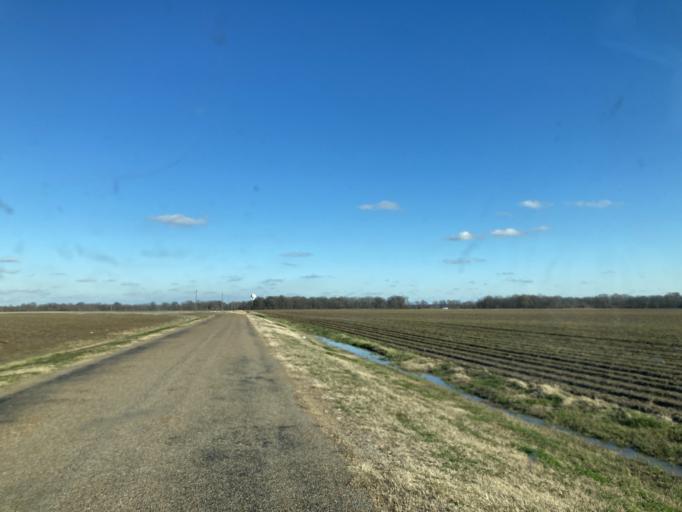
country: US
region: Mississippi
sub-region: Yazoo County
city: Yazoo City
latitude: 32.9230
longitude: -90.5092
